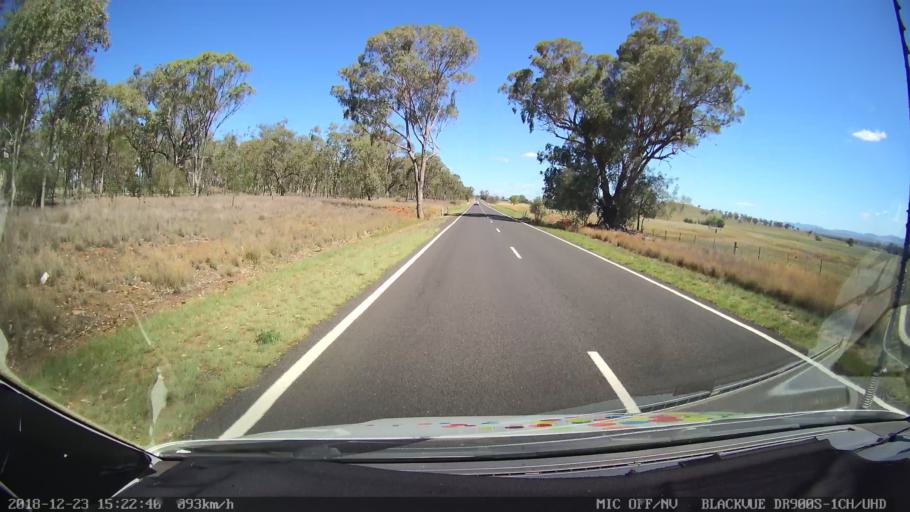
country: AU
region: New South Wales
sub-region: Tamworth Municipality
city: Manilla
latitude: -30.8710
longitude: 150.8069
